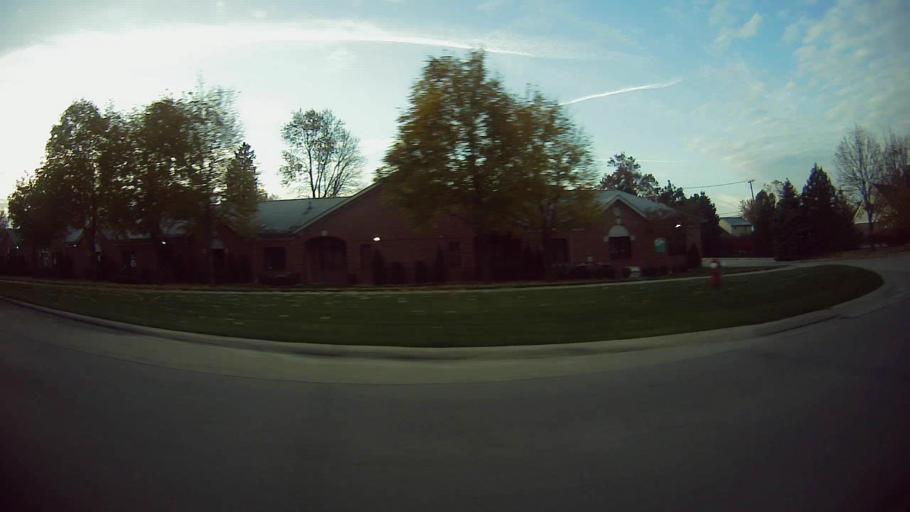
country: US
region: Michigan
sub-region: Macomb County
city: Sterling Heights
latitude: 42.5649
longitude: -83.0539
